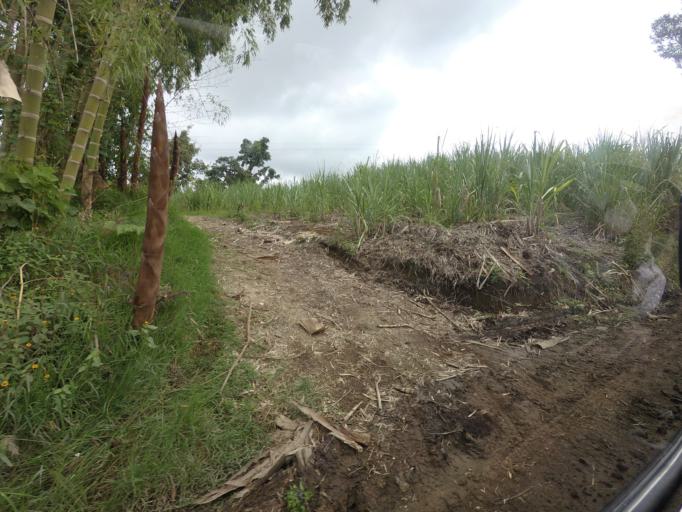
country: CO
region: Huila
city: Isnos
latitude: 1.9548
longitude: -76.2879
